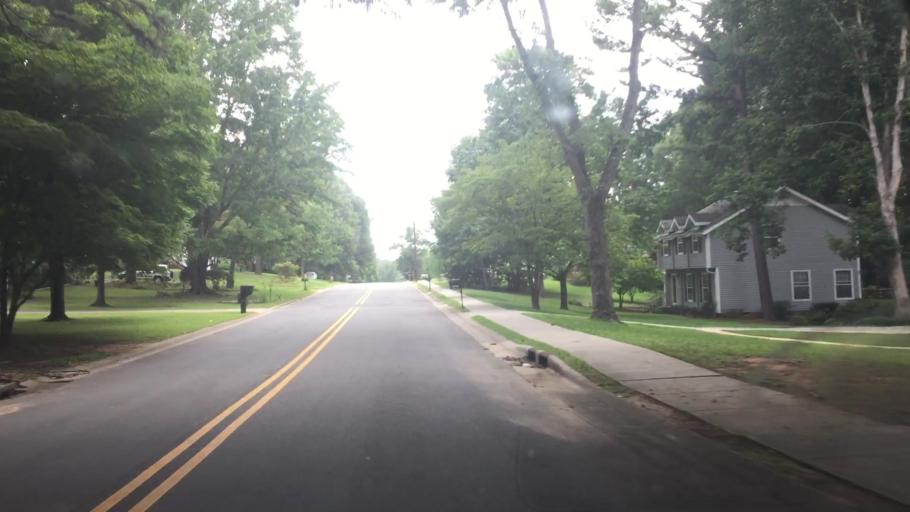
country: US
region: North Carolina
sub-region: Iredell County
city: Mooresville
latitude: 35.5560
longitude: -80.8016
